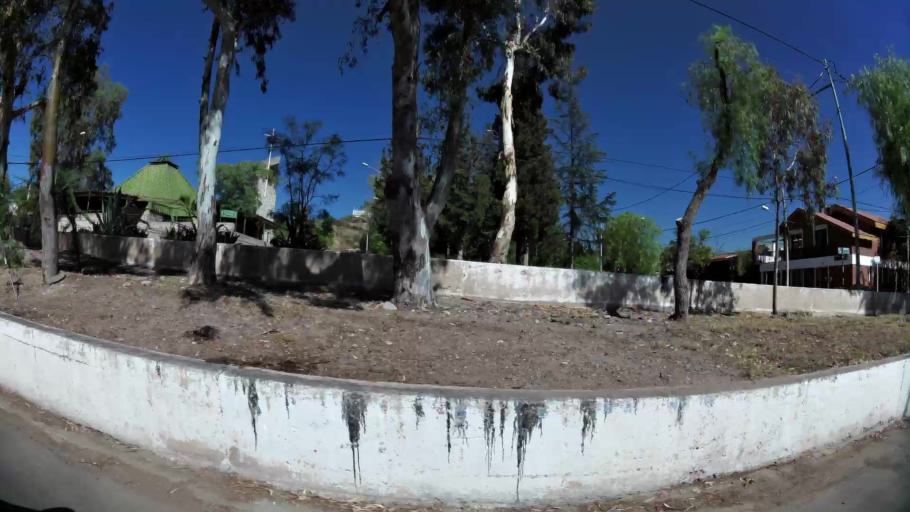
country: AR
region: Mendoza
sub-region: Departamento de Godoy Cruz
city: Godoy Cruz
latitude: -32.9021
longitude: -68.8862
